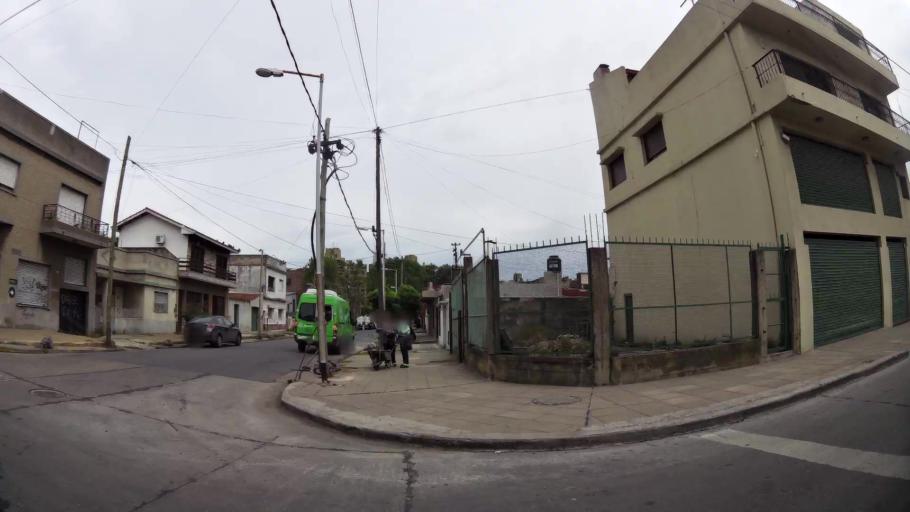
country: AR
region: Buenos Aires
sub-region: Partido de Avellaneda
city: Avellaneda
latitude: -34.6517
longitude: -58.3479
